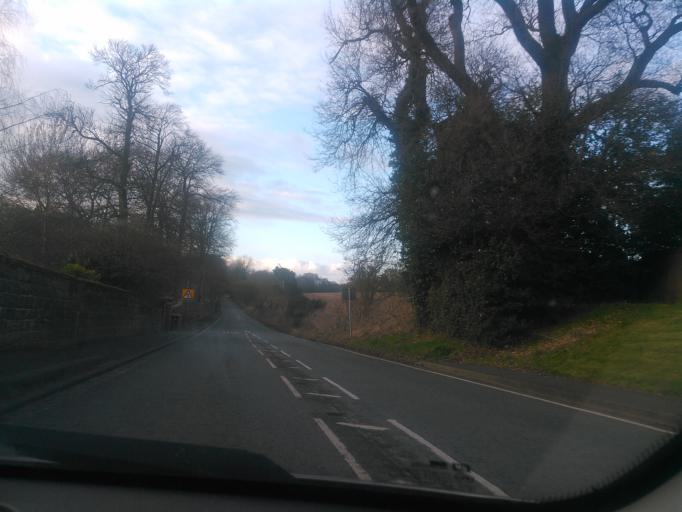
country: GB
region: England
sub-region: Telford and Wrekin
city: Newport
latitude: 52.7790
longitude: -2.3819
